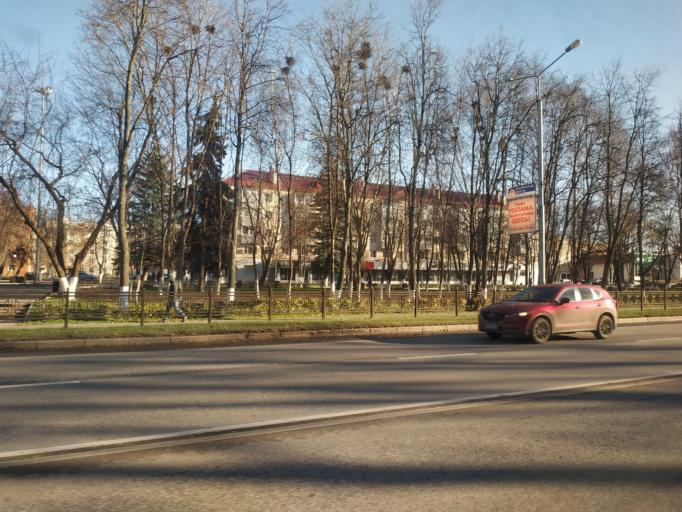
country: RU
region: Moskovskaya
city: Domodedovo
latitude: 55.4391
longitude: 37.7663
